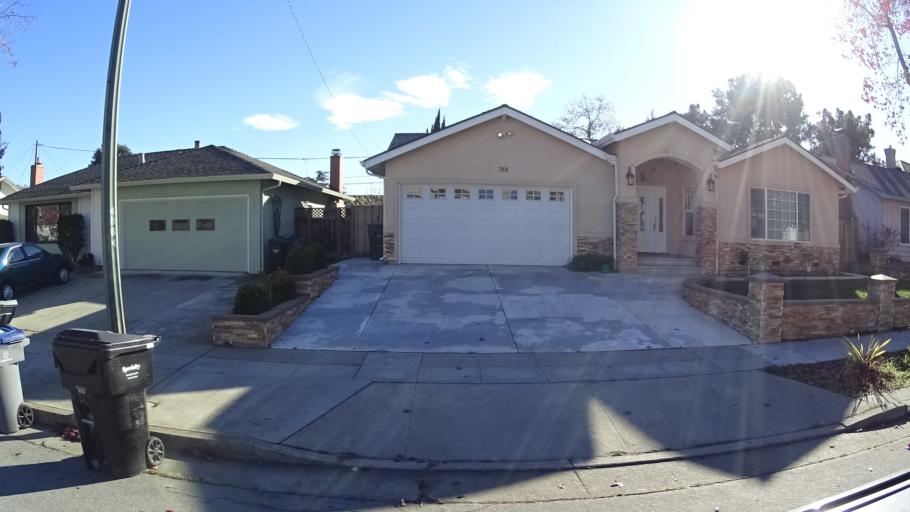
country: US
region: California
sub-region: Santa Clara County
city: Cupertino
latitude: 37.3413
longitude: -122.0202
